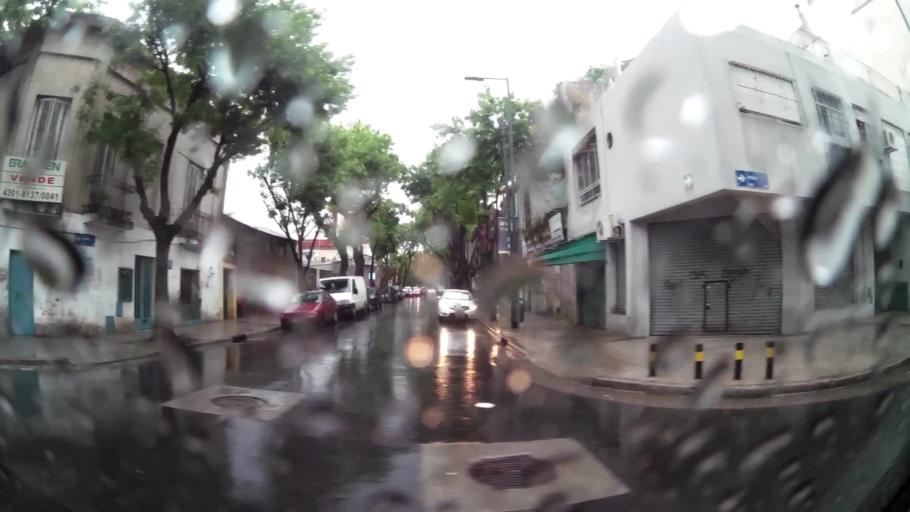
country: AR
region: Buenos Aires
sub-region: Partido de Avellaneda
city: Avellaneda
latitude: -34.6364
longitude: -58.3618
